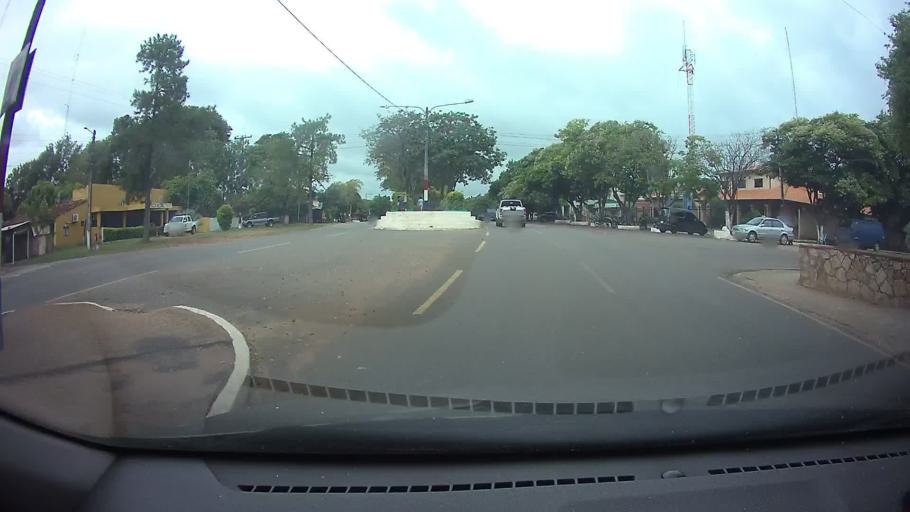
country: PY
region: Central
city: Nueva Italia
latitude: -25.6113
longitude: -57.4700
